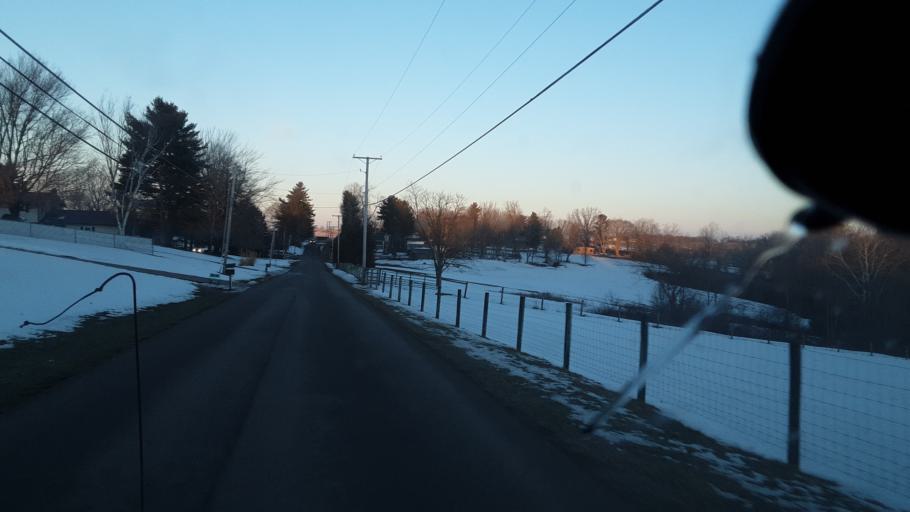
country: US
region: Ohio
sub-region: Perry County
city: Somerset
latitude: 39.8120
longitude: -82.3060
